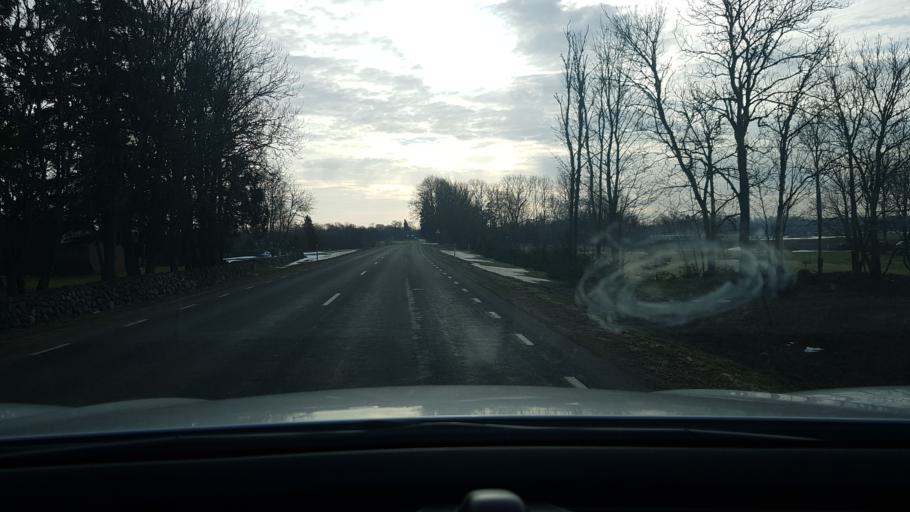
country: EE
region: Saare
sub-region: Kuressaare linn
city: Kuressaare
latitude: 58.2978
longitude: 22.5407
